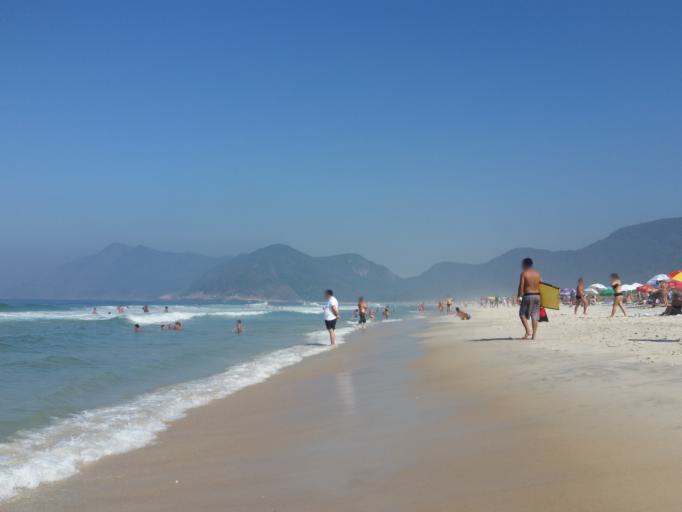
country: BR
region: Rio de Janeiro
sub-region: Nilopolis
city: Nilopolis
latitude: -23.0482
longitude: -43.5176
